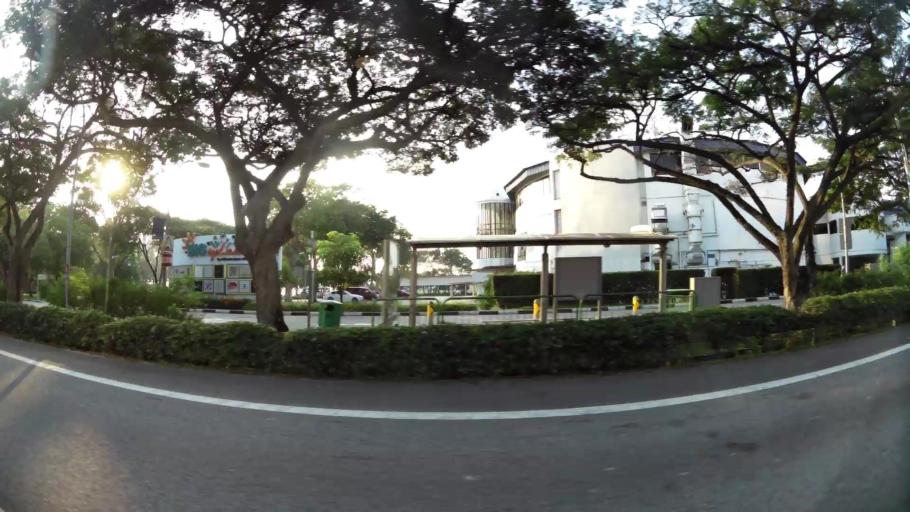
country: SG
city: Singapore
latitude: 1.2980
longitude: 103.9002
